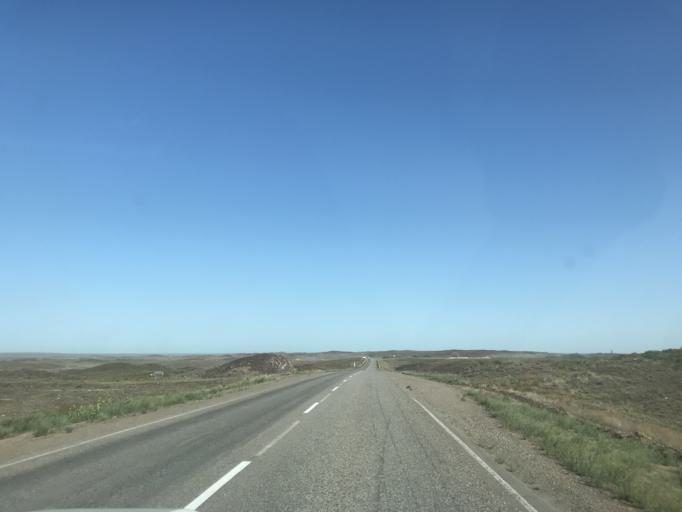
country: KZ
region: Zhambyl
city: Mynaral
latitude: 45.4611
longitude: 73.5791
